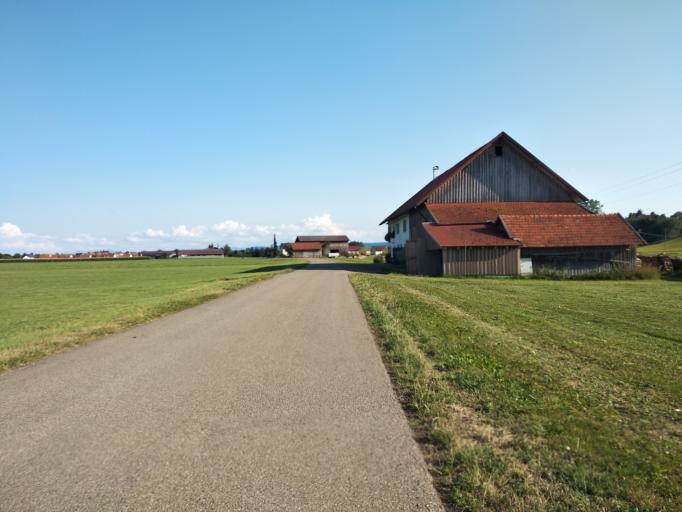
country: DE
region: Bavaria
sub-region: Swabia
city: Legau
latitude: 47.8699
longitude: 10.1183
